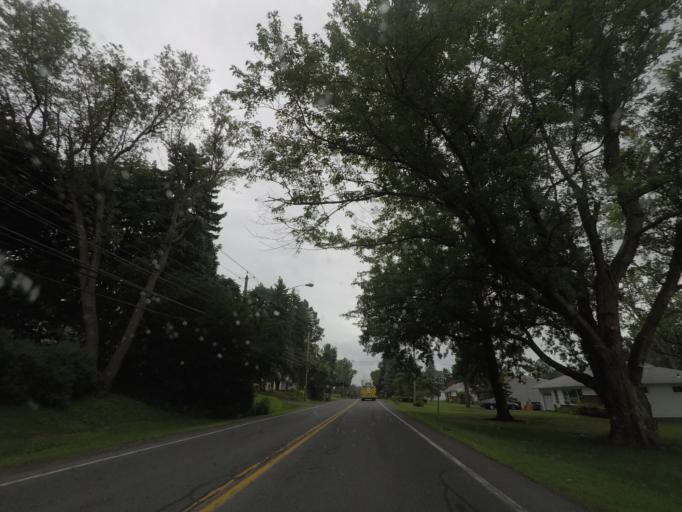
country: US
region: New York
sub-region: Albany County
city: West Albany
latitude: 42.6865
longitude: -73.7609
